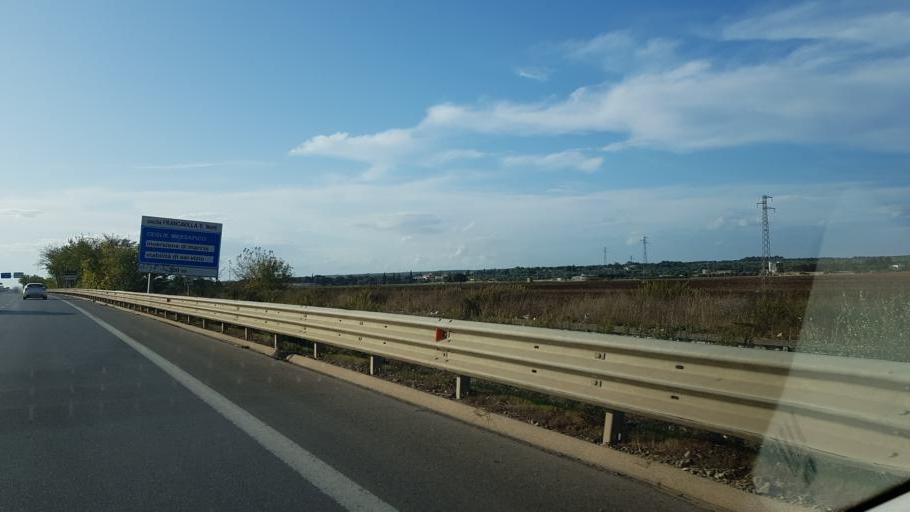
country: IT
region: Apulia
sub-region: Provincia di Brindisi
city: Francavilla Fontana
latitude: 40.5466
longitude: 17.5812
